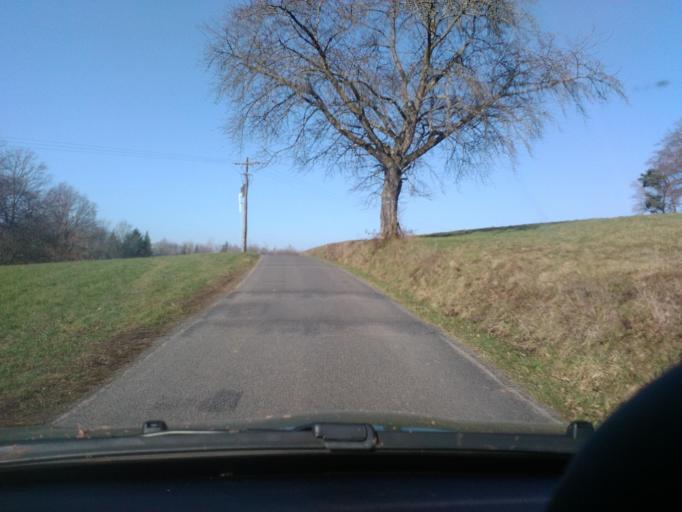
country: FR
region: Lorraine
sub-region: Departement des Vosges
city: Moyenmoutier
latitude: 48.3593
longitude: 6.9234
